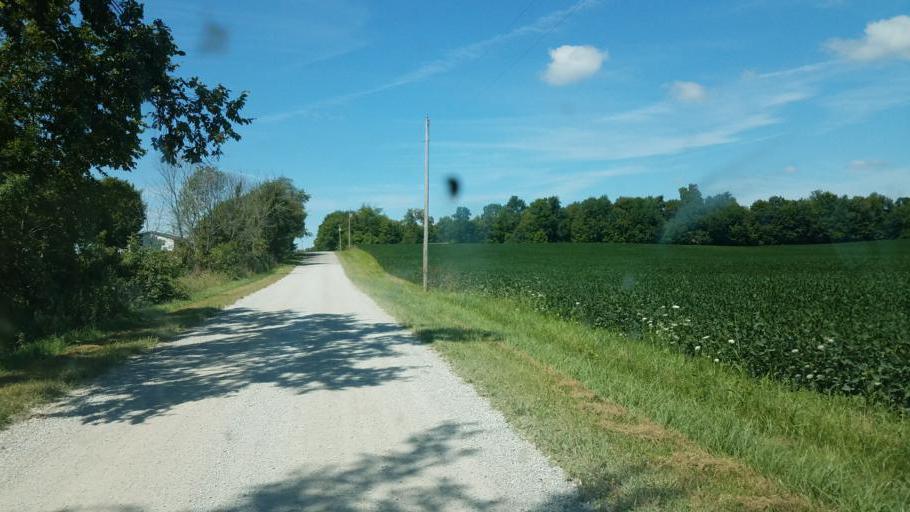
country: US
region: Ohio
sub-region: Knox County
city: Centerburg
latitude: 40.4355
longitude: -82.7302
